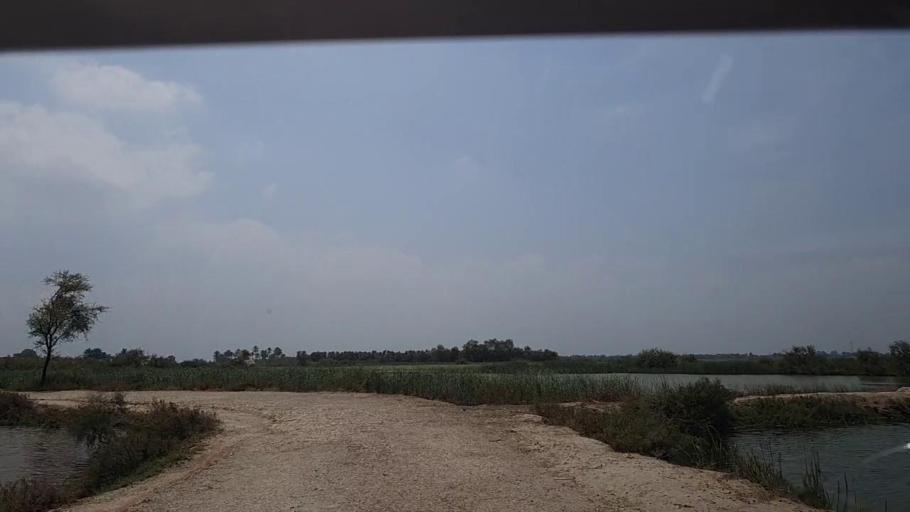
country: PK
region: Sindh
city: Khanpur
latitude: 27.8955
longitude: 69.3968
